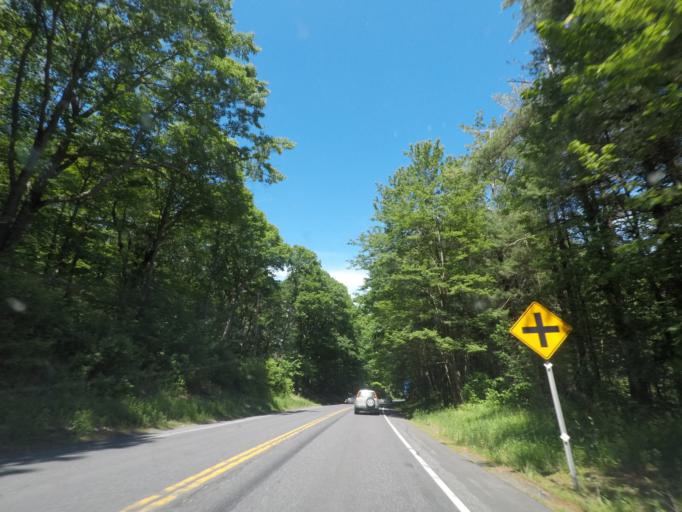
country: US
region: Massachusetts
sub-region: Berkshire County
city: West Stockbridge
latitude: 42.3329
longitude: -73.4347
